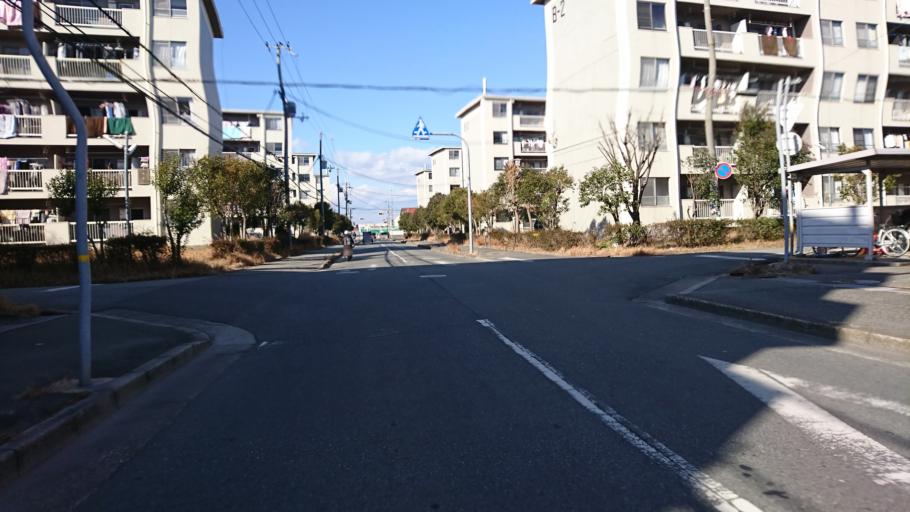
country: JP
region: Hyogo
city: Kakogawacho-honmachi
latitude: 34.7335
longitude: 134.8665
